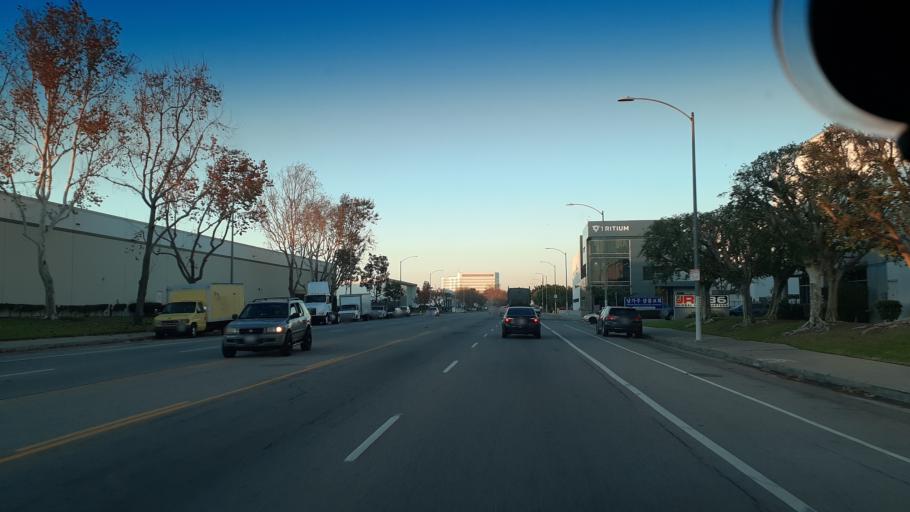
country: US
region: California
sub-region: Los Angeles County
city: Carson
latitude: 33.8477
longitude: -118.2904
